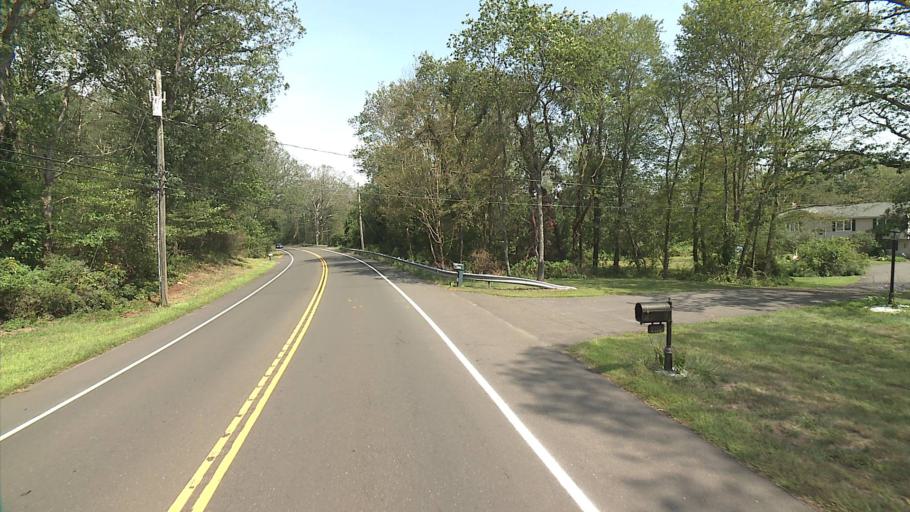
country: US
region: Connecticut
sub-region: Middlesex County
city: Durham
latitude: 41.4280
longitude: -72.6495
